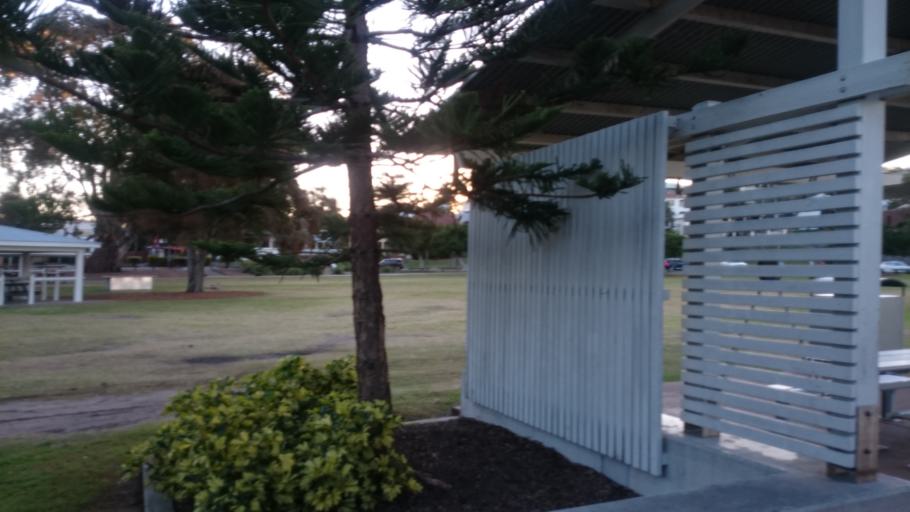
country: AU
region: Queensland
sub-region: Brisbane
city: Manly West
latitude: -27.4663
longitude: 153.1927
